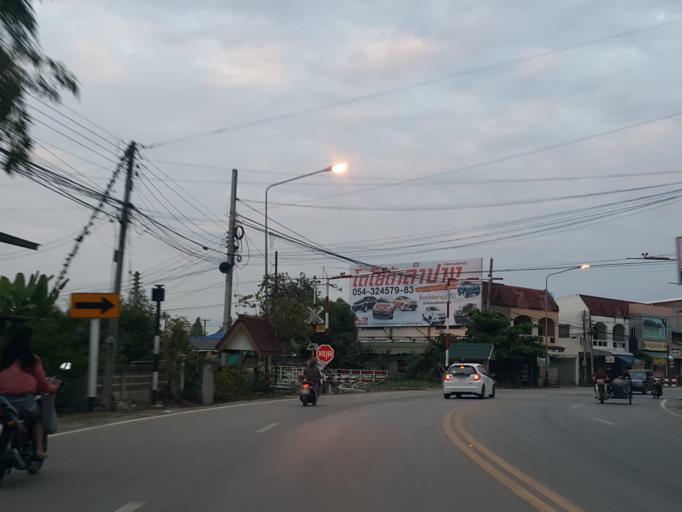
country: TH
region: Lampang
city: Lampang
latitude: 18.2554
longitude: 99.4918
